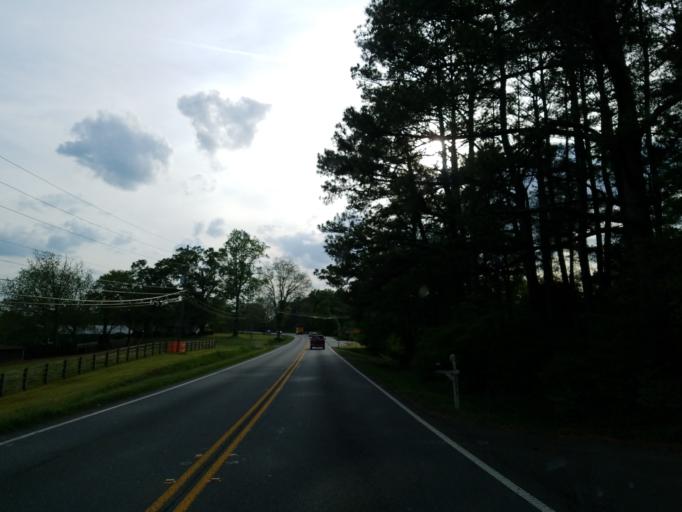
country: US
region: Georgia
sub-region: Cherokee County
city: Canton
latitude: 34.2373
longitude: -84.4375
